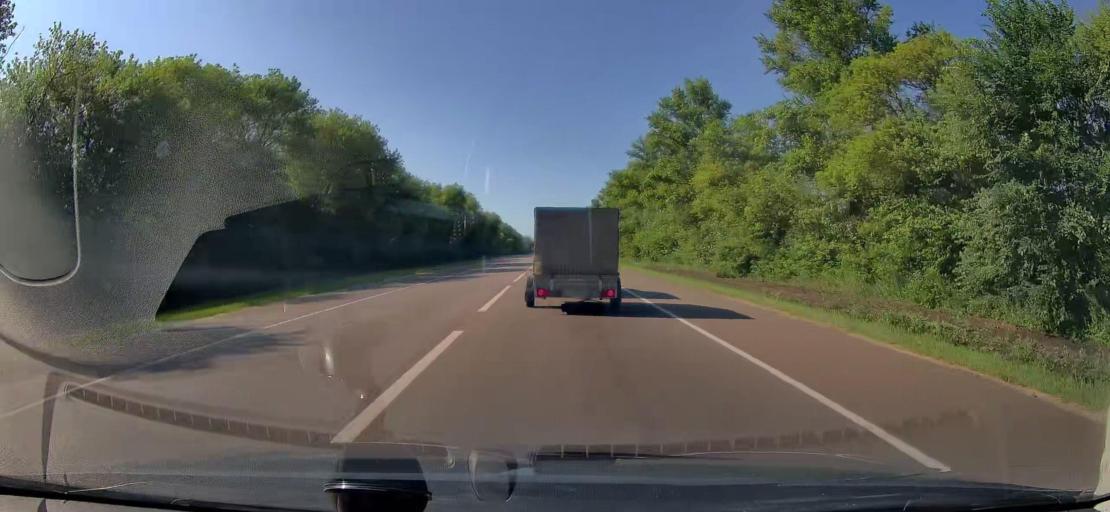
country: RU
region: Orjol
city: Kromy
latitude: 52.6108
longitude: 35.7628
